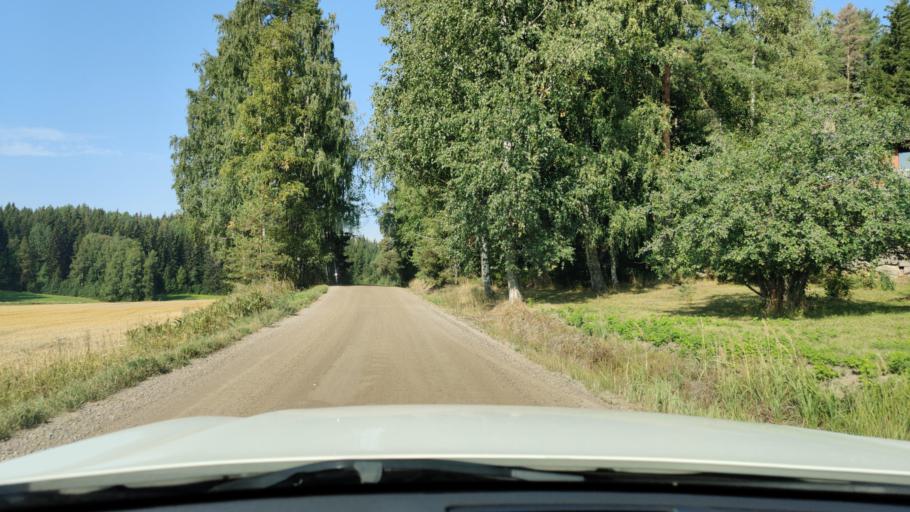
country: FI
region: Haeme
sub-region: Haemeenlinna
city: Tervakoski
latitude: 60.6748
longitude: 24.6026
